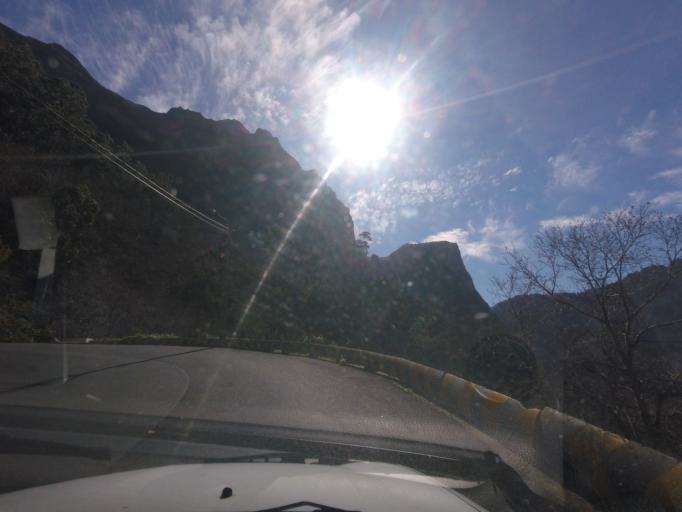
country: PT
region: Madeira
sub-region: Camara de Lobos
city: Curral das Freiras
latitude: 32.7203
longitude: -16.9636
